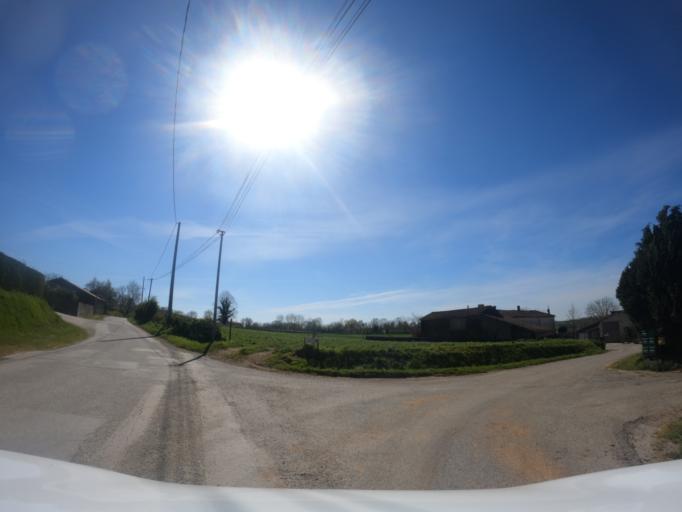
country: FR
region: Pays de la Loire
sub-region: Departement de la Vendee
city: Saint-Pierre-du-Chemin
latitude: 46.6844
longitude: -0.7038
